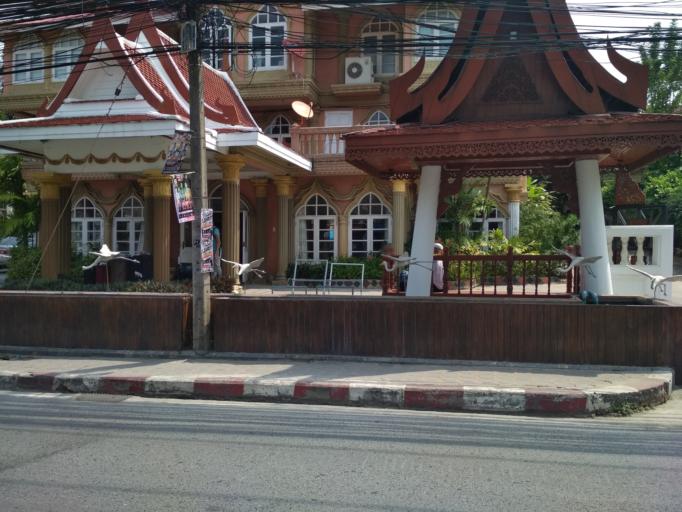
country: TH
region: Surat Thani
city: Ko Samui
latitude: 9.5184
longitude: 100.0566
